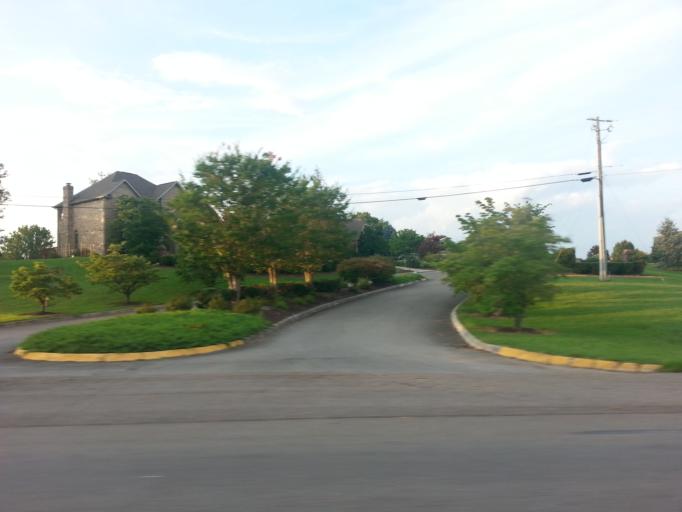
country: US
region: Tennessee
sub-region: Knox County
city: Knoxville
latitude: 36.0875
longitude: -83.9425
